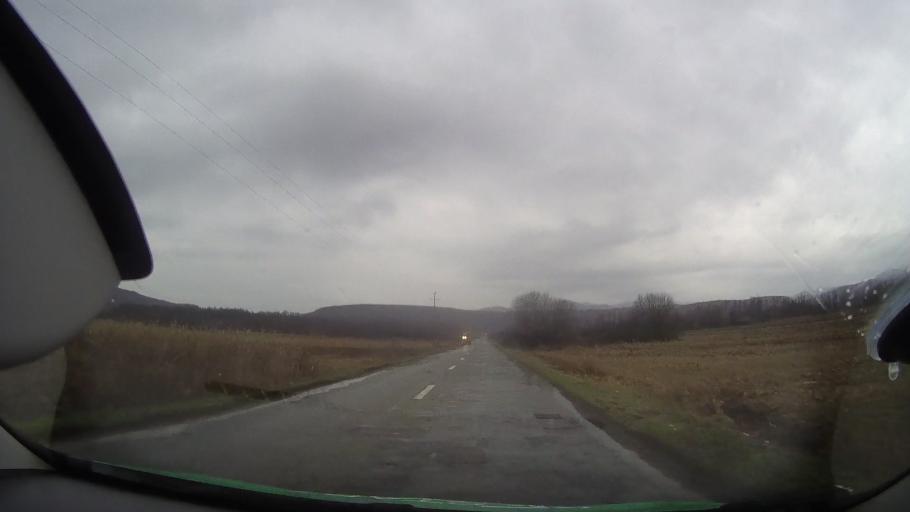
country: RO
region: Bihor
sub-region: Comuna Soimi
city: Soimi
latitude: 46.6889
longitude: 22.1043
